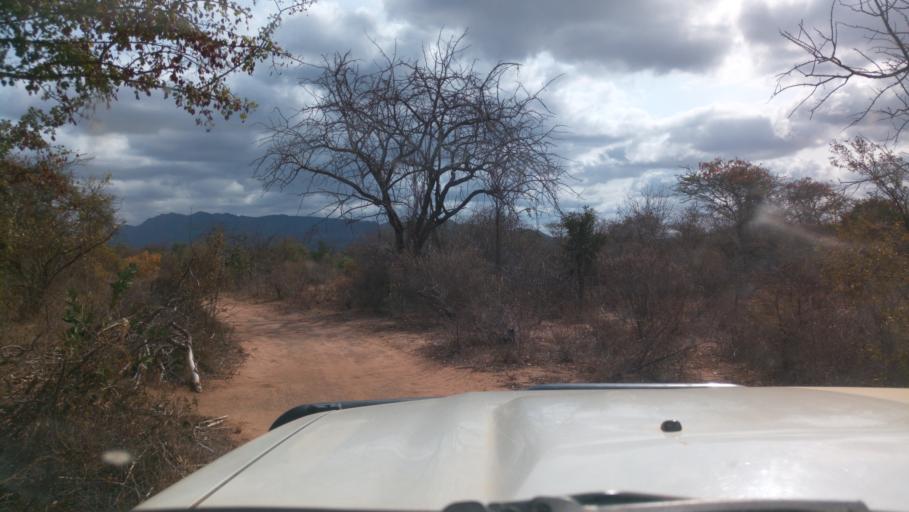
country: KE
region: Kitui
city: Kitui
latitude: -1.9896
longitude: 38.3364
